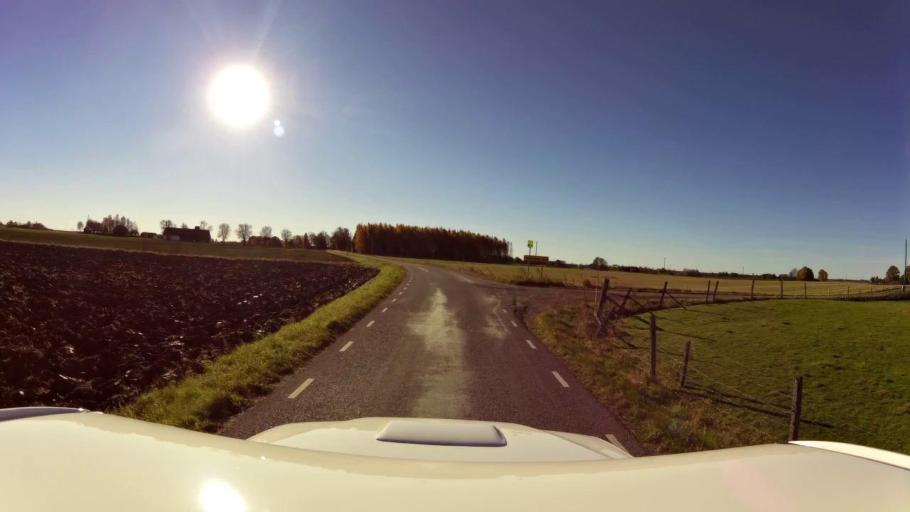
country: SE
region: OEstergoetland
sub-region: Linkopings Kommun
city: Ljungsbro
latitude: 58.4874
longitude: 15.4177
